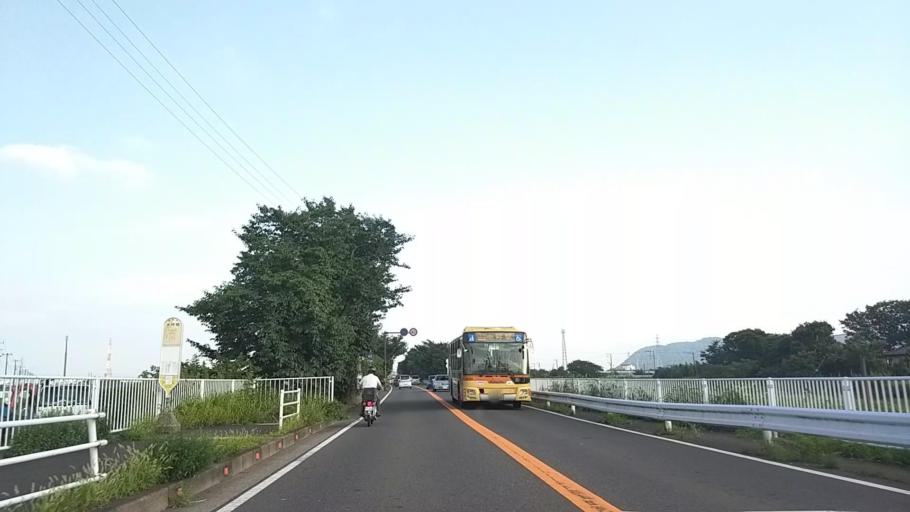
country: JP
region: Kanagawa
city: Isehara
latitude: 35.3540
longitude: 139.3103
